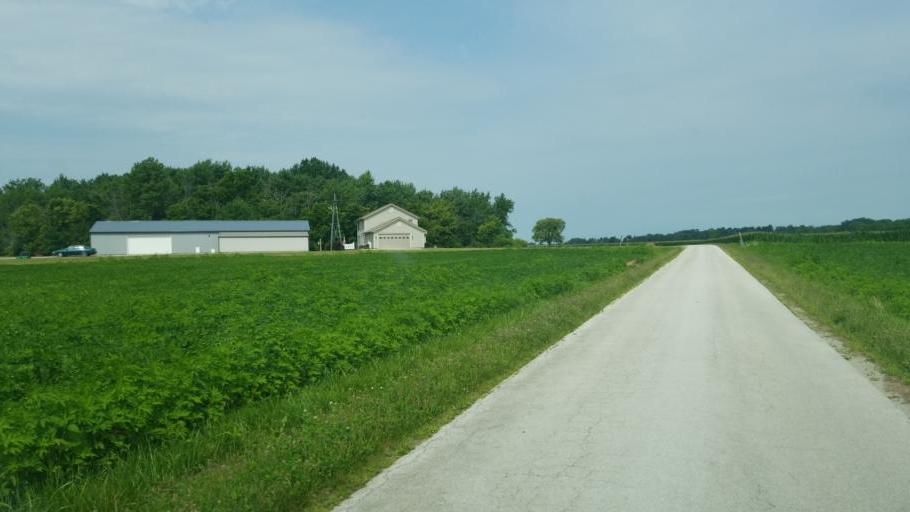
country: US
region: Ohio
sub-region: Wyandot County
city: Upper Sandusky
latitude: 40.8471
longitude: -83.3655
